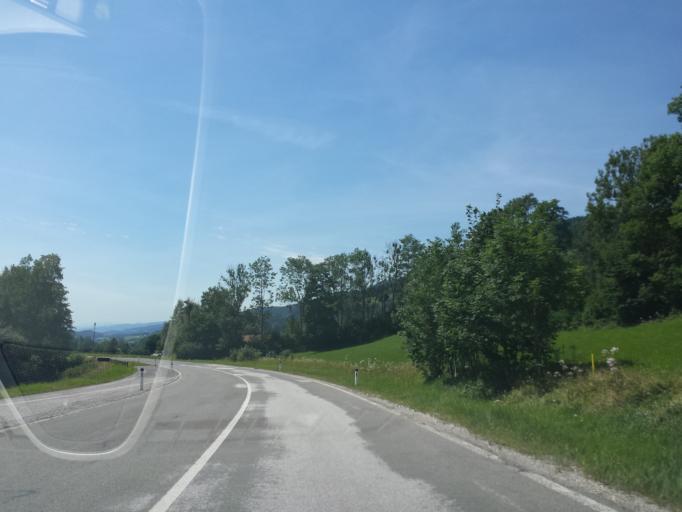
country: AT
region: Lower Austria
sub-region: Politischer Bezirk Neunkirchen
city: Semmering
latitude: 47.6254
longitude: 15.7992
